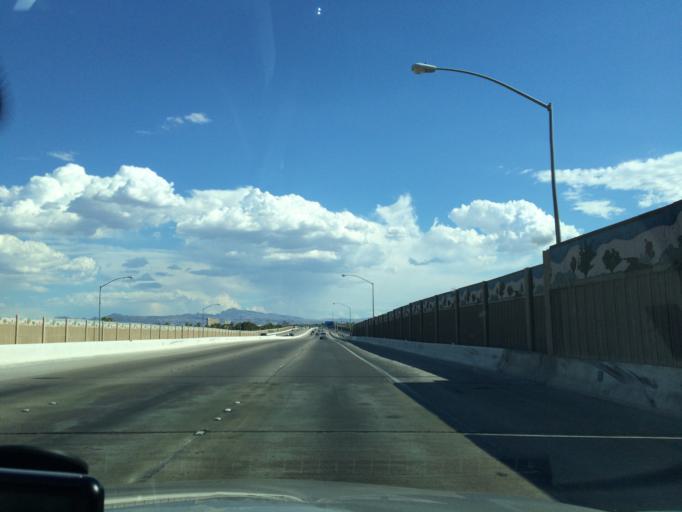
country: US
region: Nevada
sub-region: Clark County
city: Winchester
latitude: 36.1589
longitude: -115.0918
